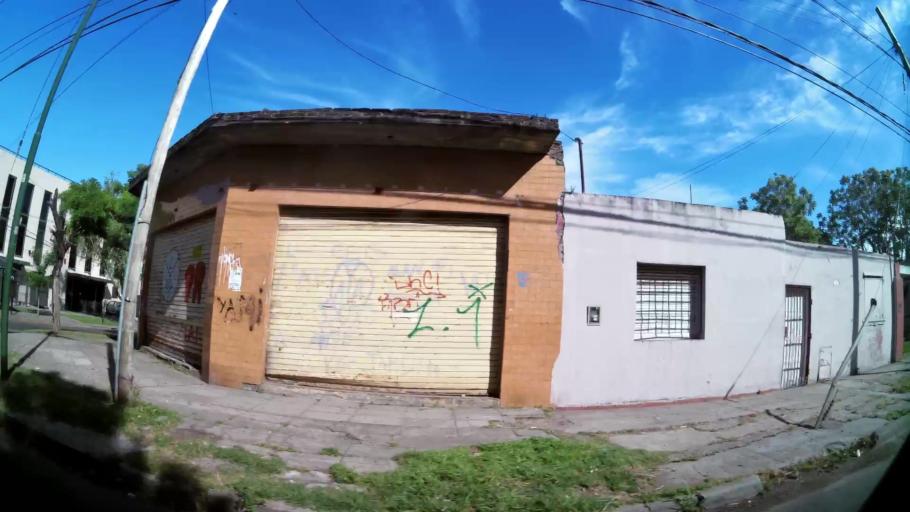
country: AR
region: Buenos Aires
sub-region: Partido de Tigre
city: Tigre
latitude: -34.4808
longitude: -58.5805
